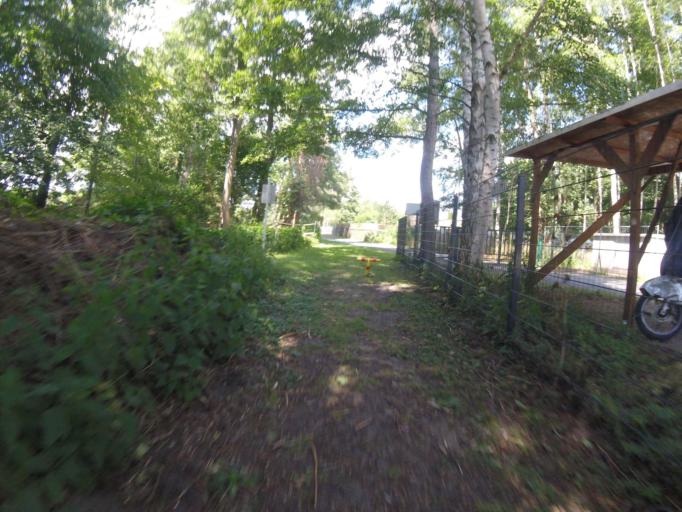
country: DE
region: Brandenburg
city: Wildau
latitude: 52.3269
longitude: 13.6445
